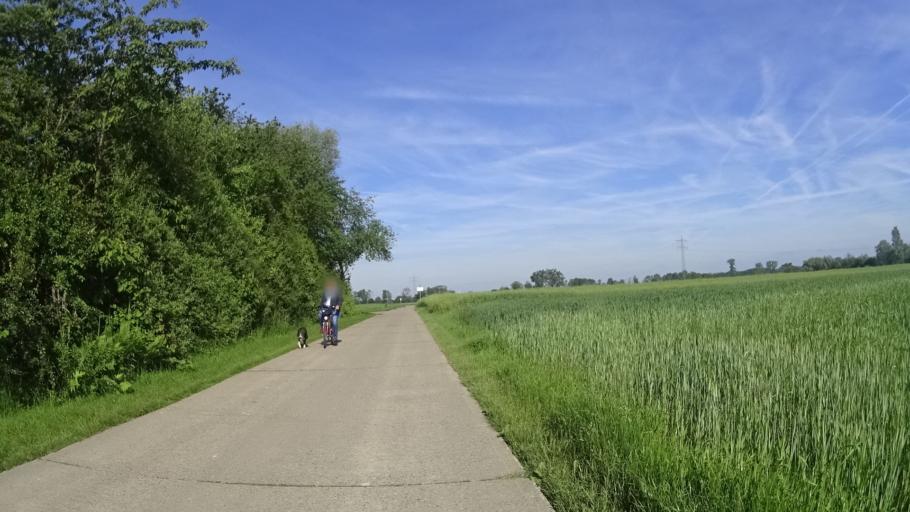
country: DE
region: Baden-Wuerttemberg
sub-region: Freiburg Region
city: Kehl
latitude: 48.5768
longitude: 7.8565
